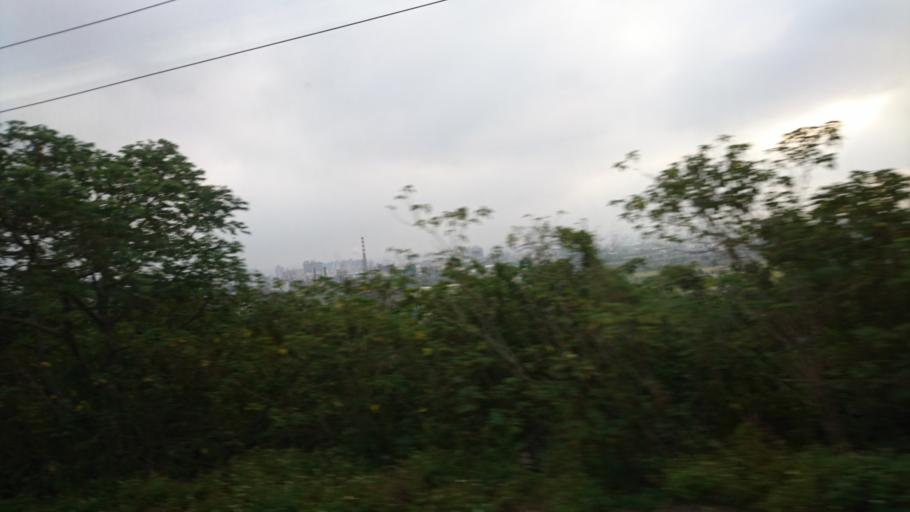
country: TW
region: Taiwan
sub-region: Hsinchu
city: Zhubei
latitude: 24.8584
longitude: 121.0003
